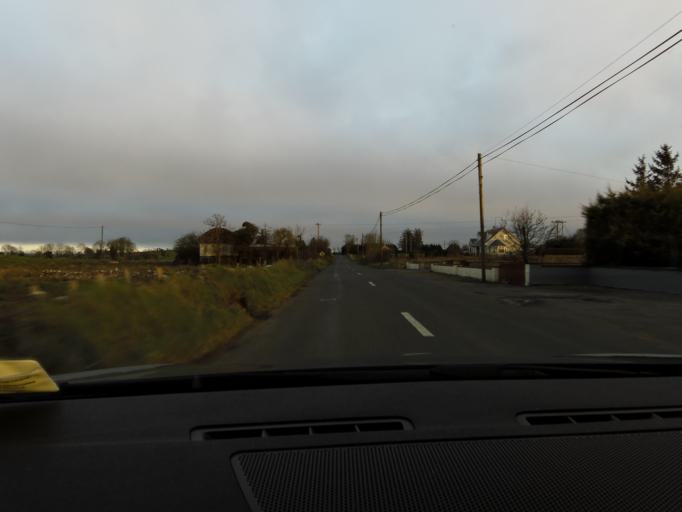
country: IE
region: Connaught
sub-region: Sligo
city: Ballymote
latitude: 54.0225
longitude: -8.5656
